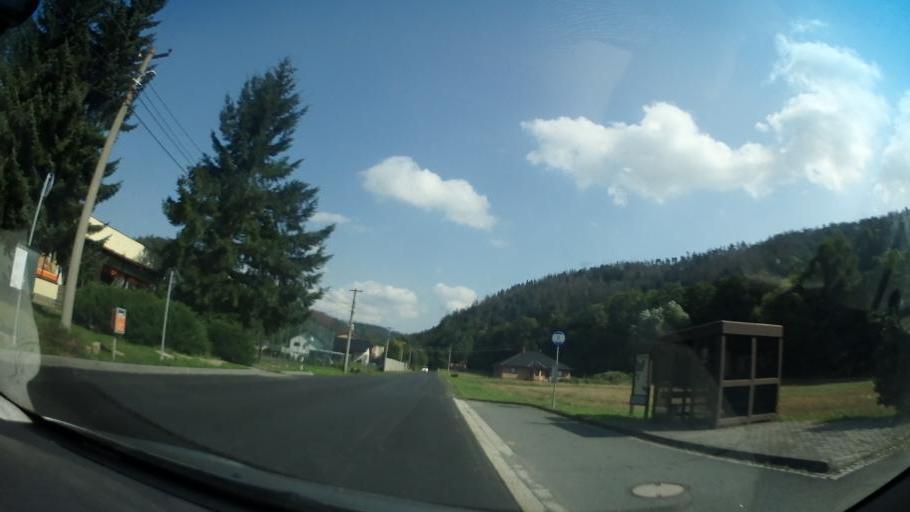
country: CZ
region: South Moravian
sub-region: Okres Brno-Venkov
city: Nedvedice
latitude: 49.5280
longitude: 16.3485
